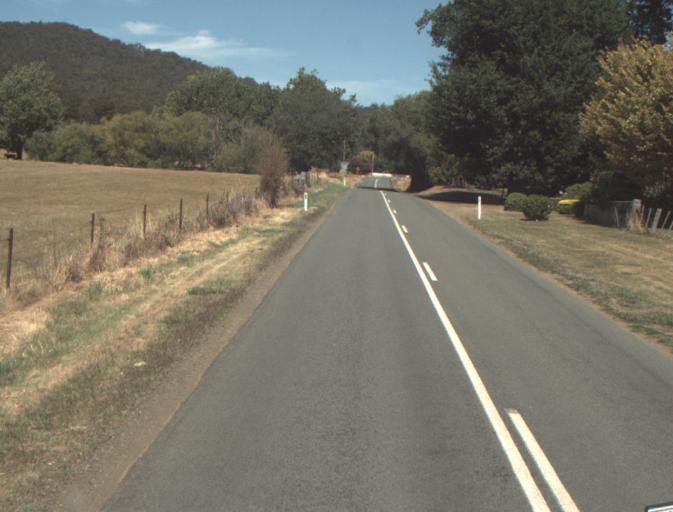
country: AU
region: Tasmania
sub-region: Launceston
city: Mayfield
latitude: -41.2629
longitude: 147.1352
